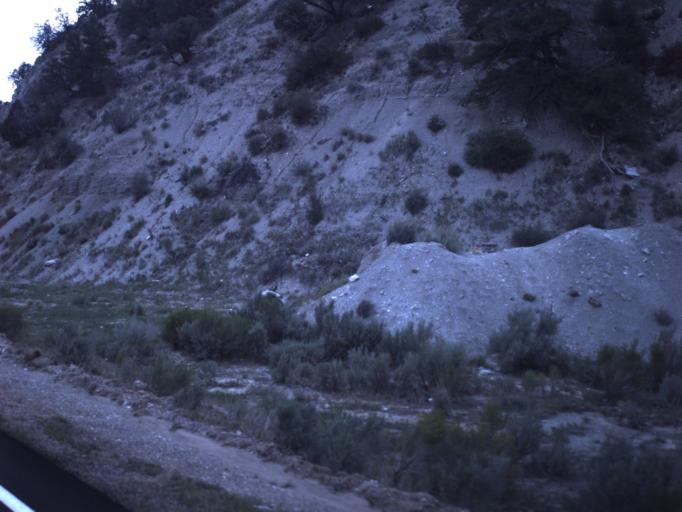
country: US
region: Utah
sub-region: Duchesne County
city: Duchesne
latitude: 39.9768
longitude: -110.6189
